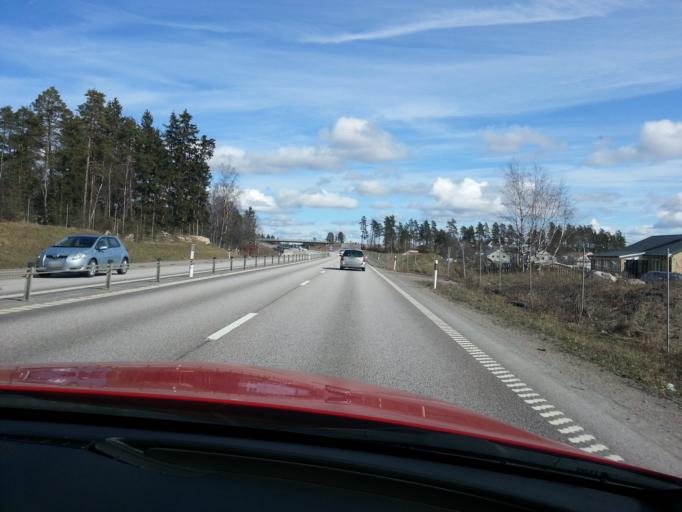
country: SE
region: Uppsala
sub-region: Uppsala Kommun
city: Storvreta
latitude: 59.9100
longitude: 17.7324
